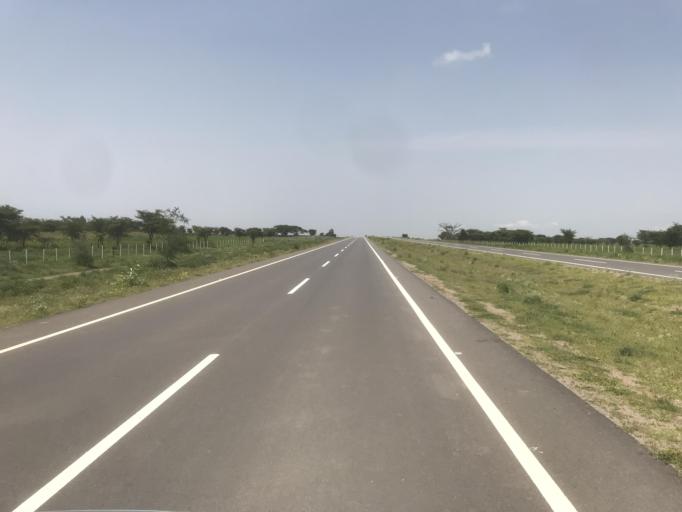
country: ET
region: Oromiya
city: Mojo
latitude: 8.3676
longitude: 38.9947
